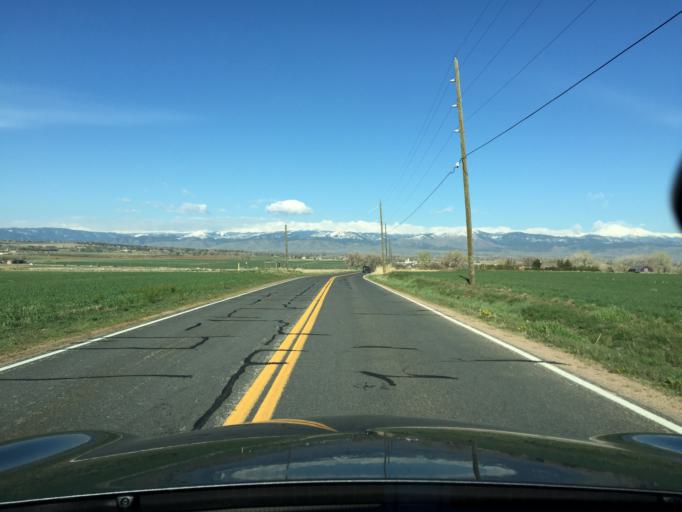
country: US
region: Colorado
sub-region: Boulder County
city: Longmont
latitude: 40.1166
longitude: -105.0903
